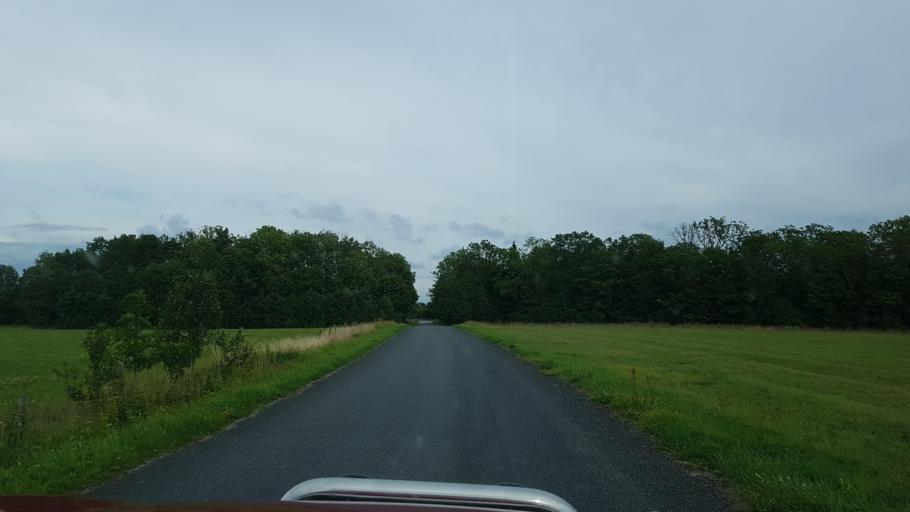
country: EE
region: Laeaene
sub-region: Ridala Parish
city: Uuemoisa
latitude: 58.9767
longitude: 23.7783
